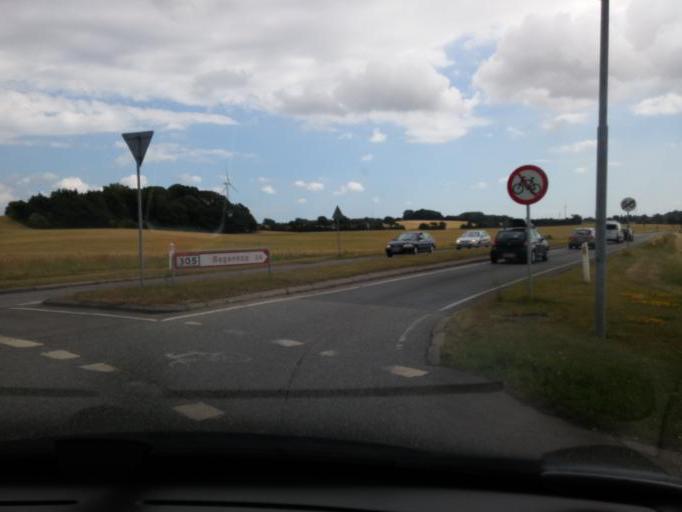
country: DK
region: South Denmark
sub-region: Langeland Kommune
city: Rudkobing
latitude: 54.9332
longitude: 10.7383
